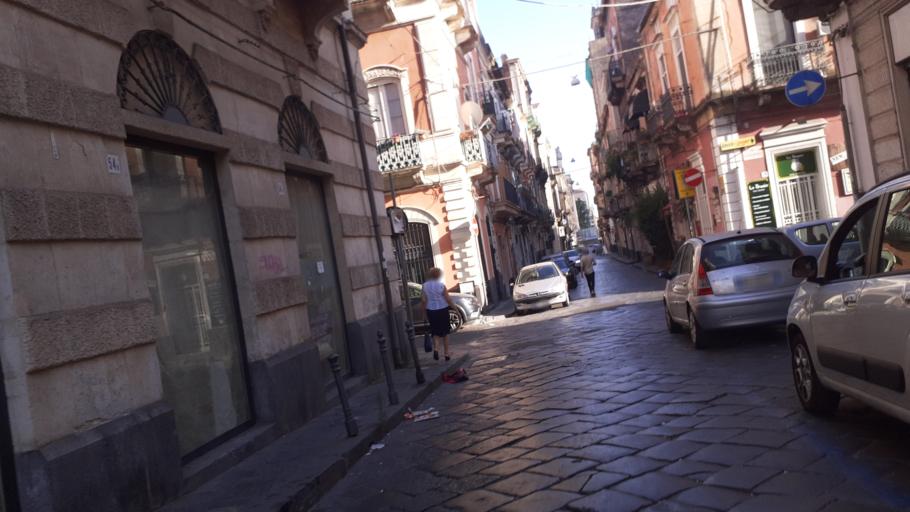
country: IT
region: Sicily
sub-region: Catania
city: Catania
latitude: 37.5123
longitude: 15.0881
